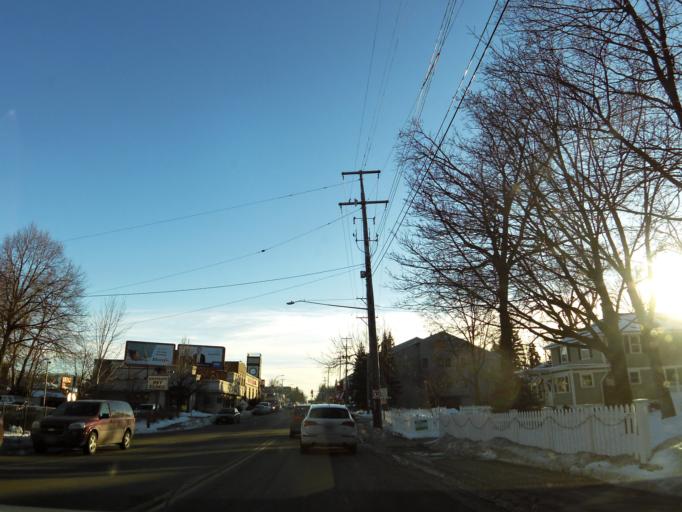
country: US
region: Minnesota
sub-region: Hennepin County
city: Saint Louis Park
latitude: 44.9240
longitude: -93.3291
